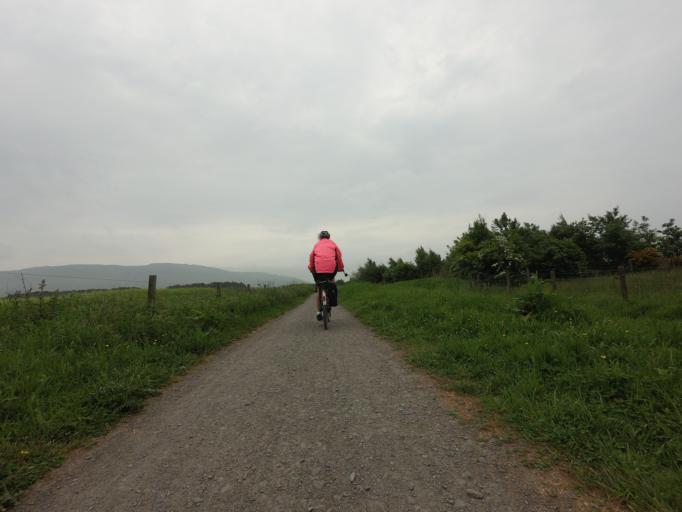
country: GB
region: Scotland
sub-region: Perth and Kinross
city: Milnathort
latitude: 56.2162
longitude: -3.3672
